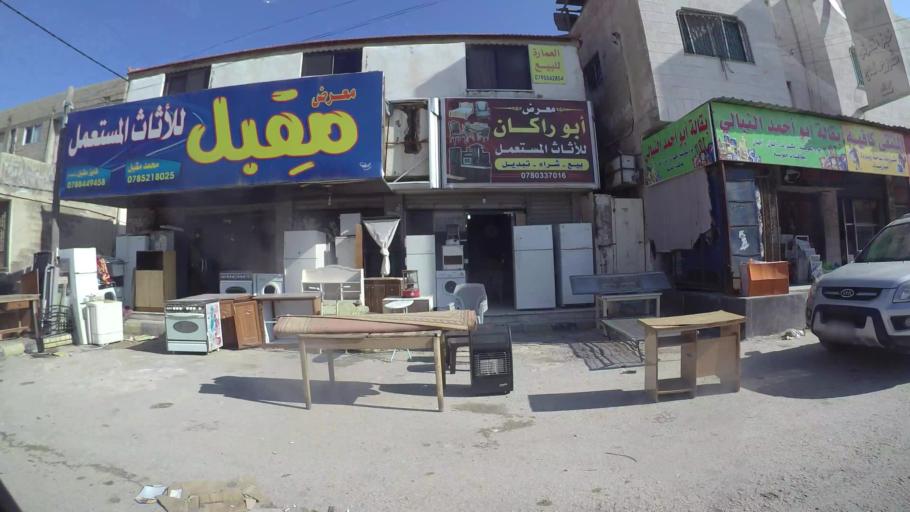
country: JO
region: Amman
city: Al Jubayhah
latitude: 32.0771
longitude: 35.8401
